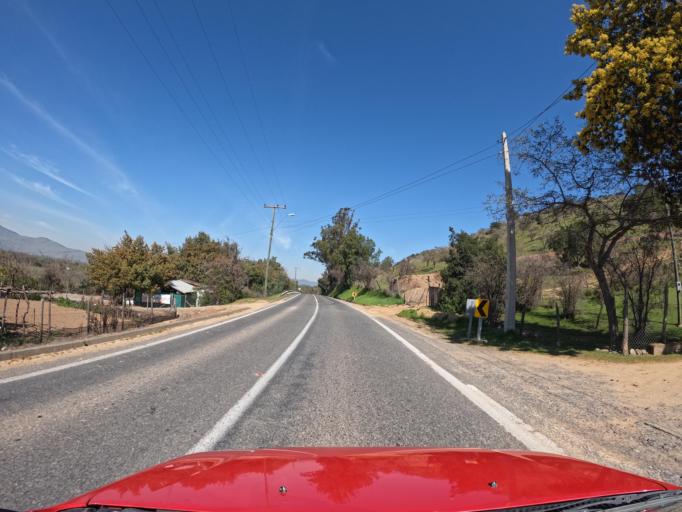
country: CL
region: Maule
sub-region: Provincia de Curico
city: Rauco
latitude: -35.0575
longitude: -71.6152
